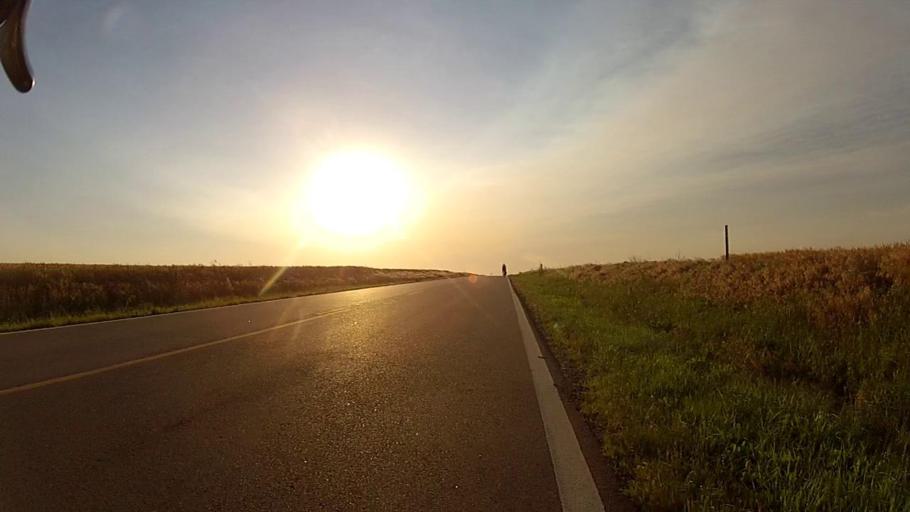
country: US
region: Kansas
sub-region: Harper County
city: Anthony
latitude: 37.1531
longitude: -97.9178
